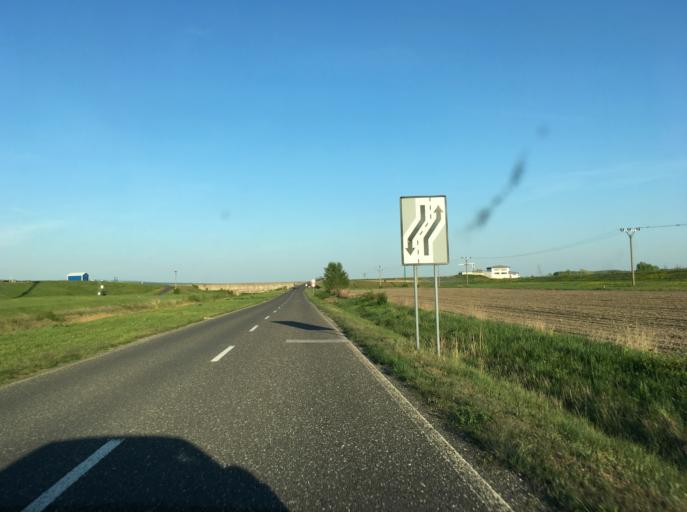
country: SK
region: Trnavsky
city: Samorin
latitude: 47.9928
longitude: 17.3478
